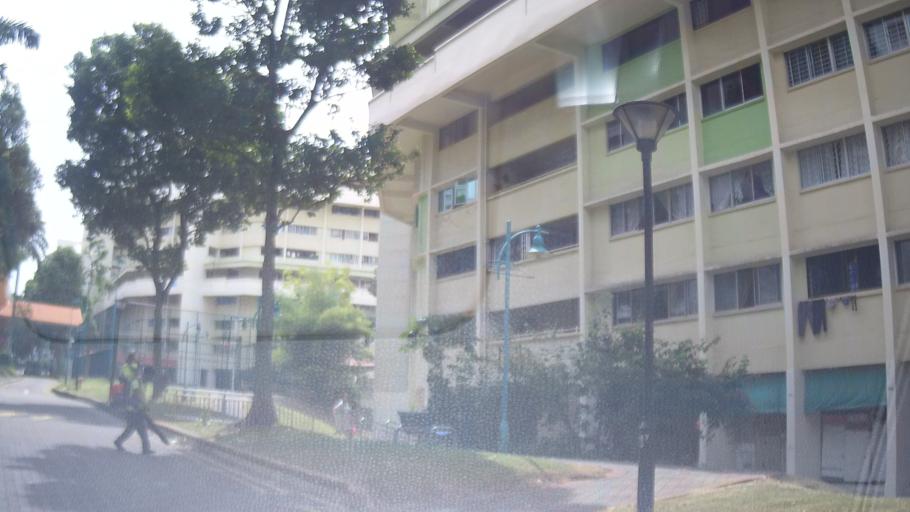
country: SG
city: Singapore
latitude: 1.3517
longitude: 103.8882
